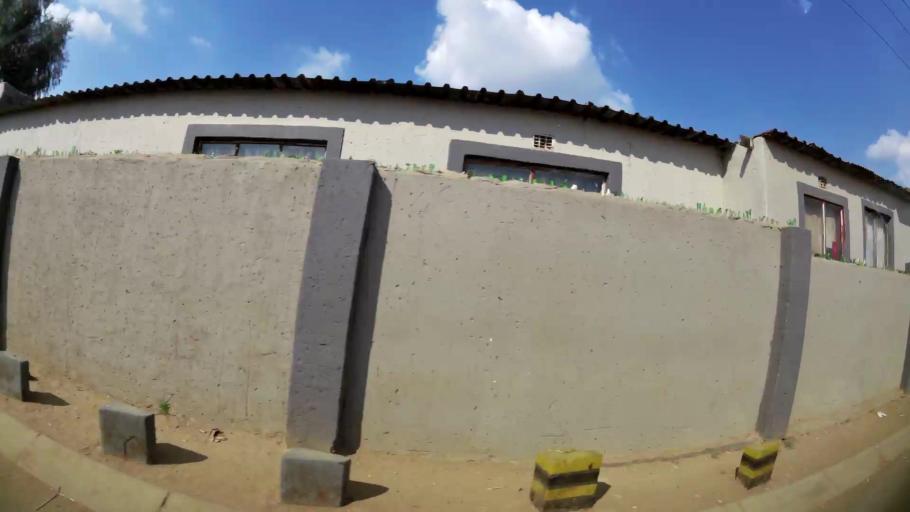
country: ZA
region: Gauteng
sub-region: Ekurhuleni Metropolitan Municipality
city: Springs
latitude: -26.1296
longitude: 28.4820
